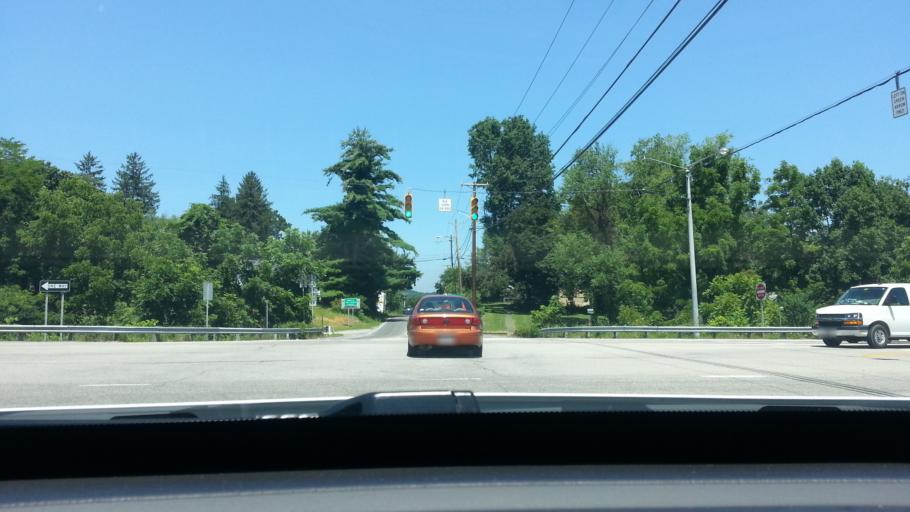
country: US
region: West Virginia
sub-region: Fayette County
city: Fayetteville
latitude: 38.0574
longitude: -81.1051
